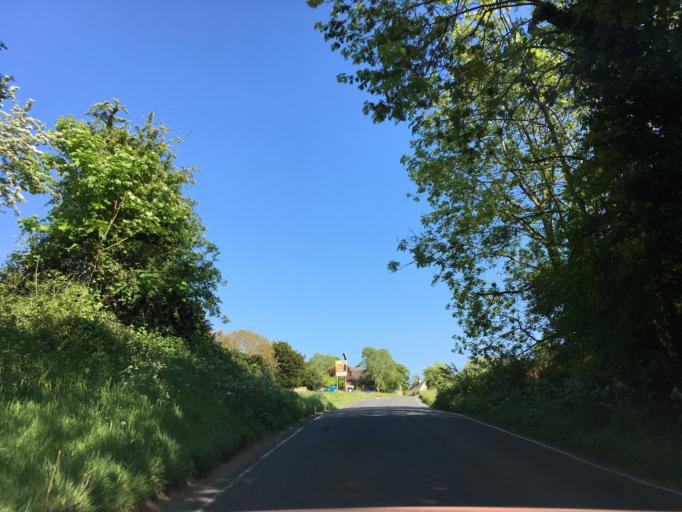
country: GB
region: England
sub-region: Gloucestershire
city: Nailsworth
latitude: 51.7114
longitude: -2.2212
